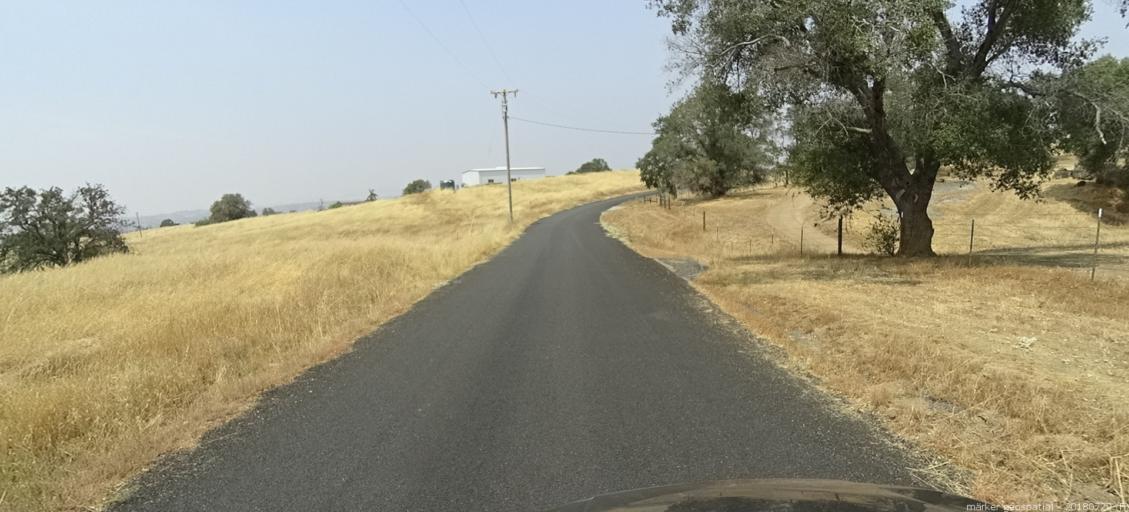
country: US
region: California
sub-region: Madera County
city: Yosemite Lakes
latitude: 37.2366
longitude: -119.9135
